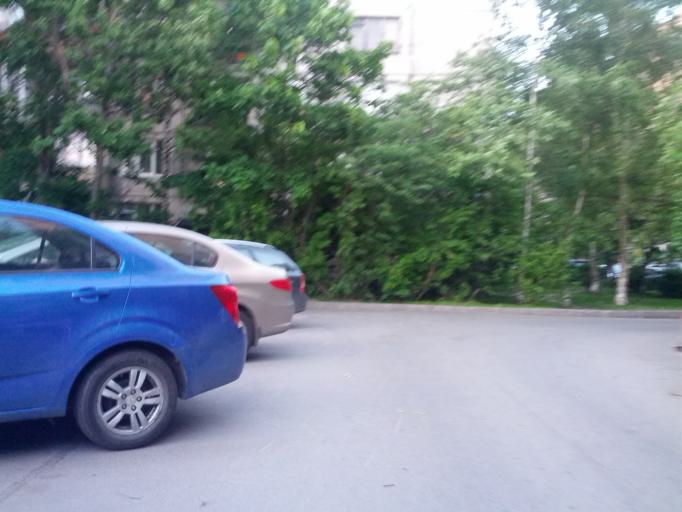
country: RU
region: St.-Petersburg
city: Krasnogvargeisky
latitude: 59.9064
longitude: 30.4776
